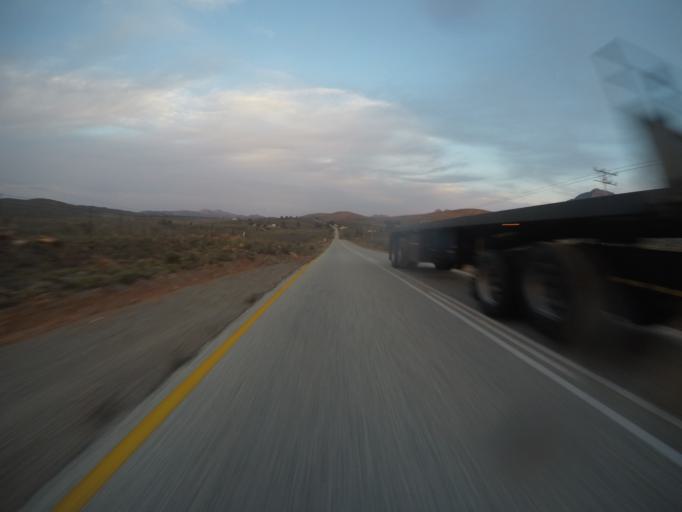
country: ZA
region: Western Cape
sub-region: Eden District Municipality
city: Plettenberg Bay
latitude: -33.7315
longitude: 23.3993
